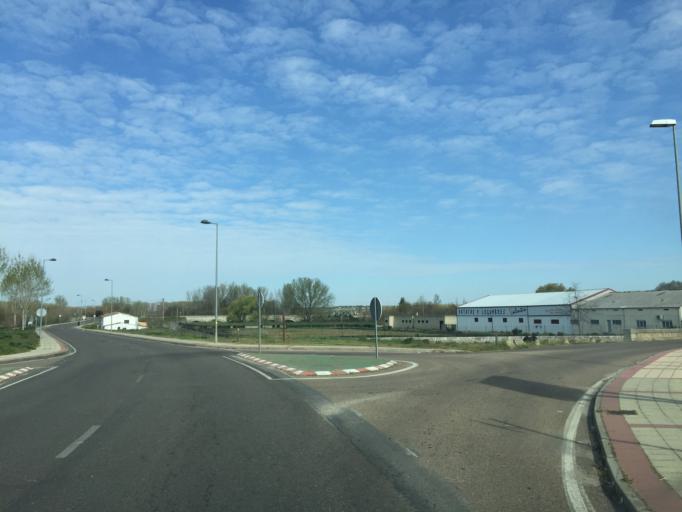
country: ES
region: Castille and Leon
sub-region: Provincia de Salamanca
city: Ciudad Rodrigo
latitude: 40.5921
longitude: -6.5387
